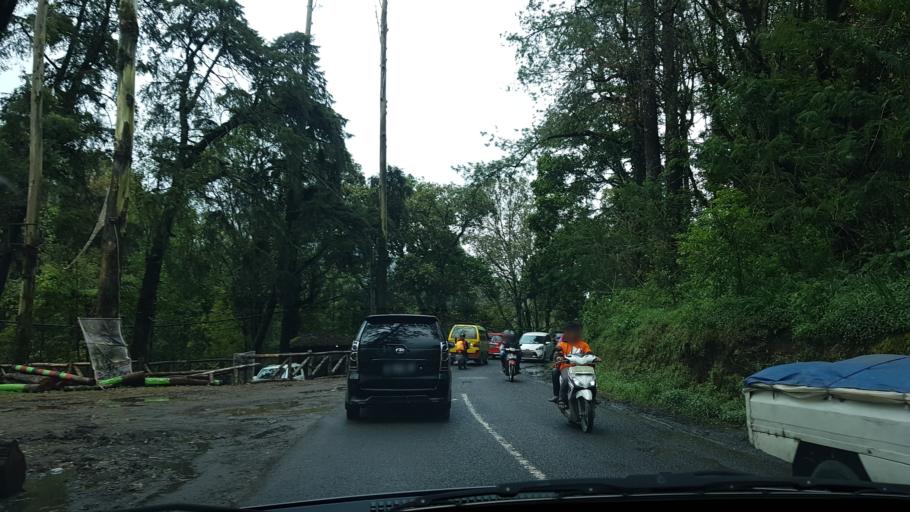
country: ID
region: West Java
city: Banjar
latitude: -7.1441
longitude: 107.3914
